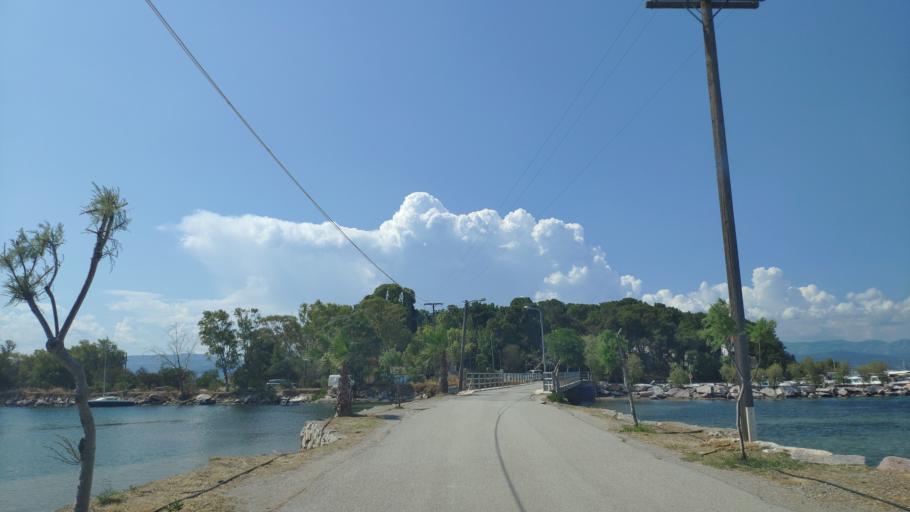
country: GR
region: Central Greece
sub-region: Nomos Evvoias
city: Eretria
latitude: 38.3870
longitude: 23.8009
